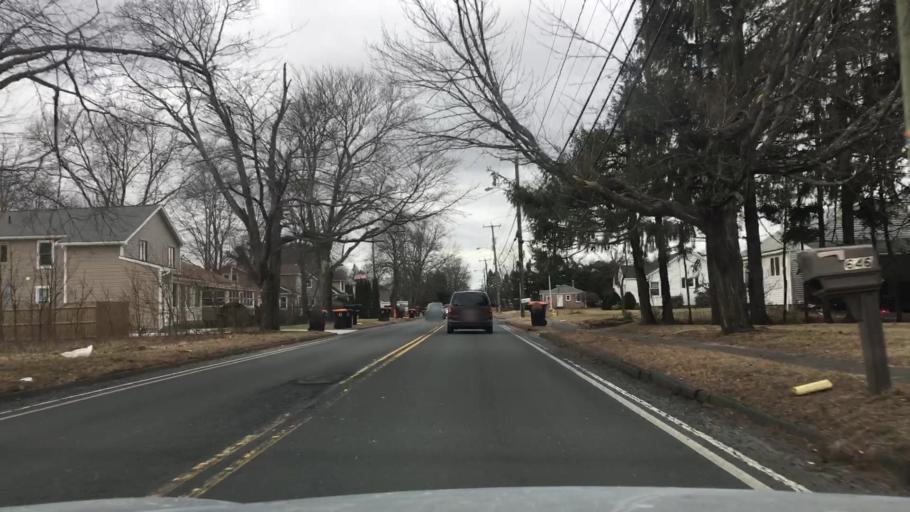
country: US
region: Massachusetts
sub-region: Hampden County
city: Agawam
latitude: 42.0704
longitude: -72.6558
